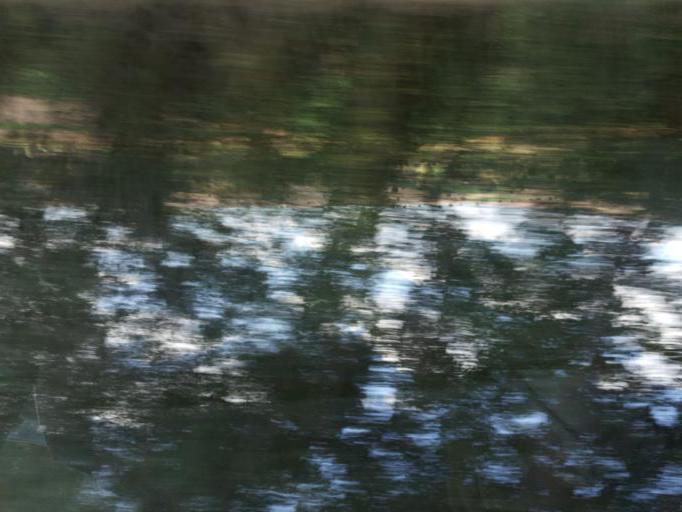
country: TR
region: Tokat
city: Camlibel
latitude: 40.1774
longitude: 36.4441
